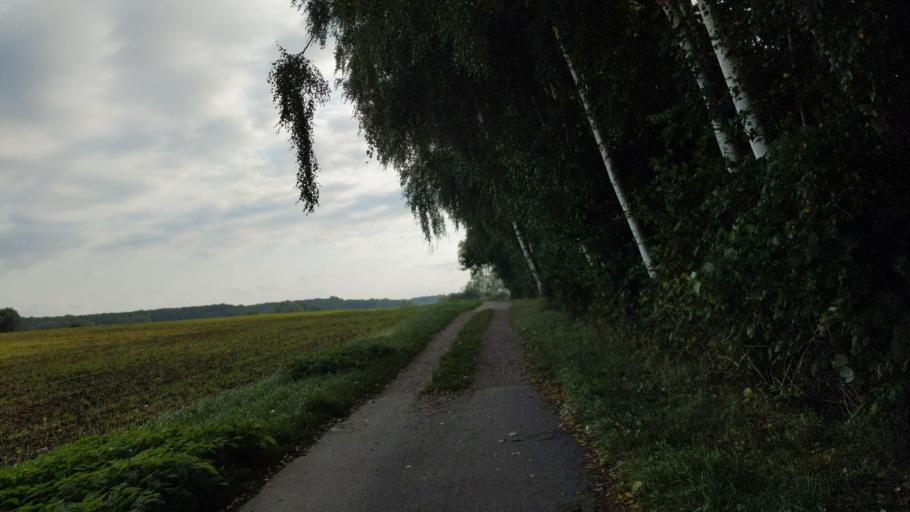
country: DE
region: Mecklenburg-Vorpommern
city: Dassow
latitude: 53.9758
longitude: 10.9615
